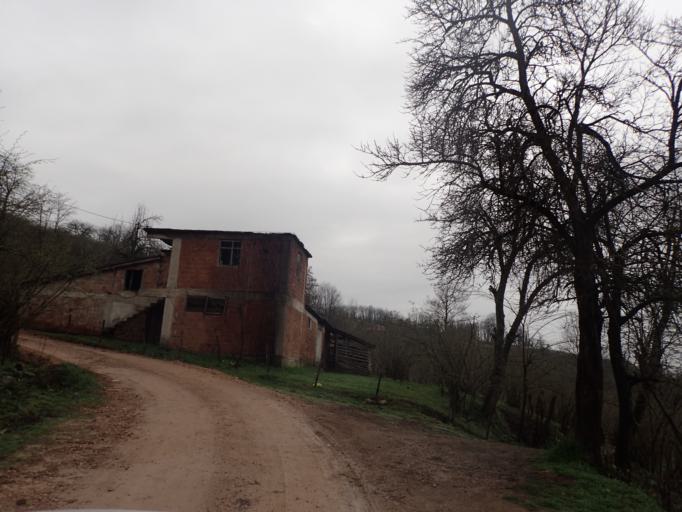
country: TR
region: Ordu
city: Camas
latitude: 40.9279
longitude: 37.5110
